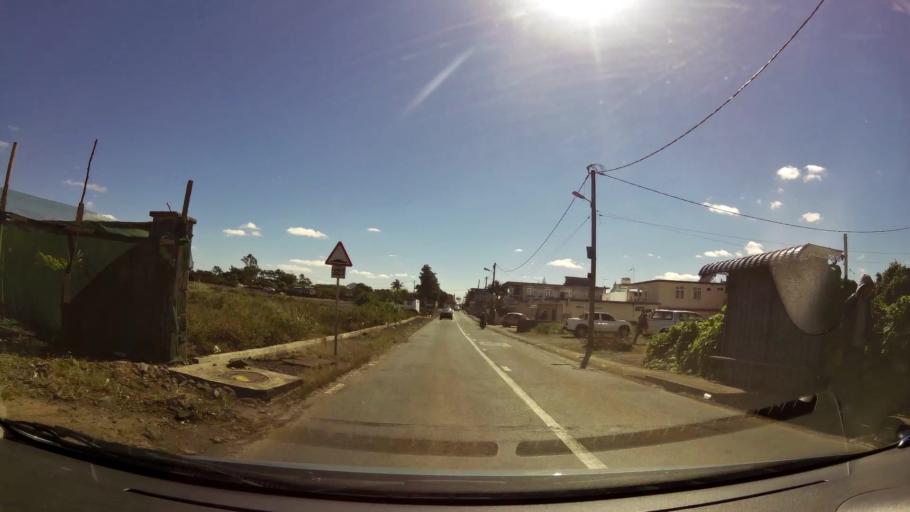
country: MU
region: Plaines Wilhems
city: Vacoas
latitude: -20.3293
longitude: 57.4864
